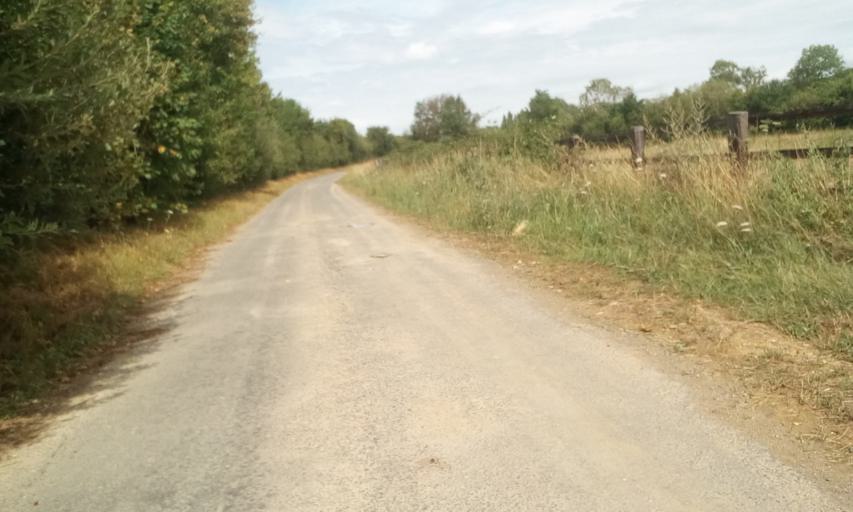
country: FR
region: Lower Normandy
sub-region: Departement du Calvados
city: Herouvillette
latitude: 49.2208
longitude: -0.2378
